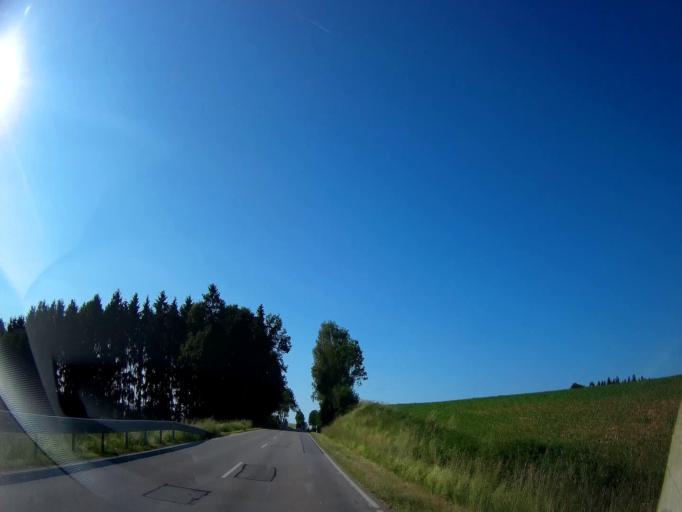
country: DE
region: Bavaria
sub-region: Lower Bavaria
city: Zeilarn
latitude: 48.3303
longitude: 12.8266
